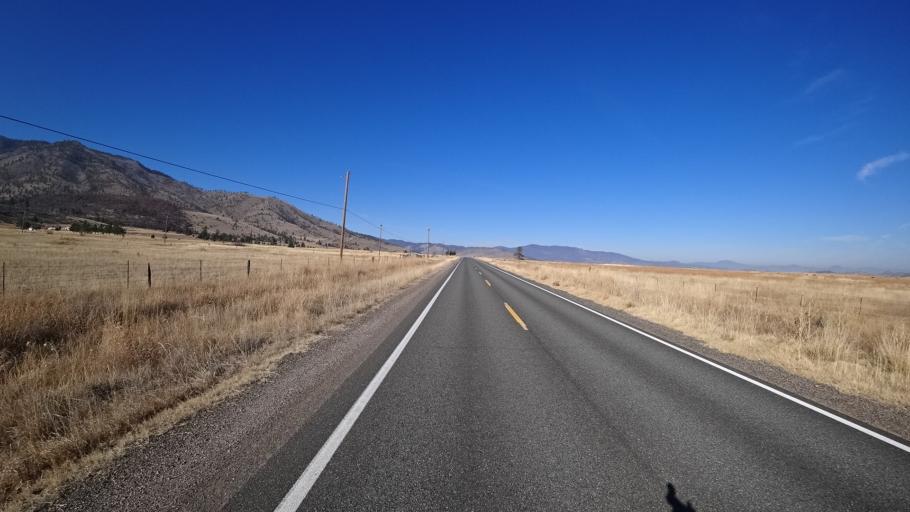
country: US
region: California
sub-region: Siskiyou County
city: Weed
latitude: 41.4731
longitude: -122.4824
